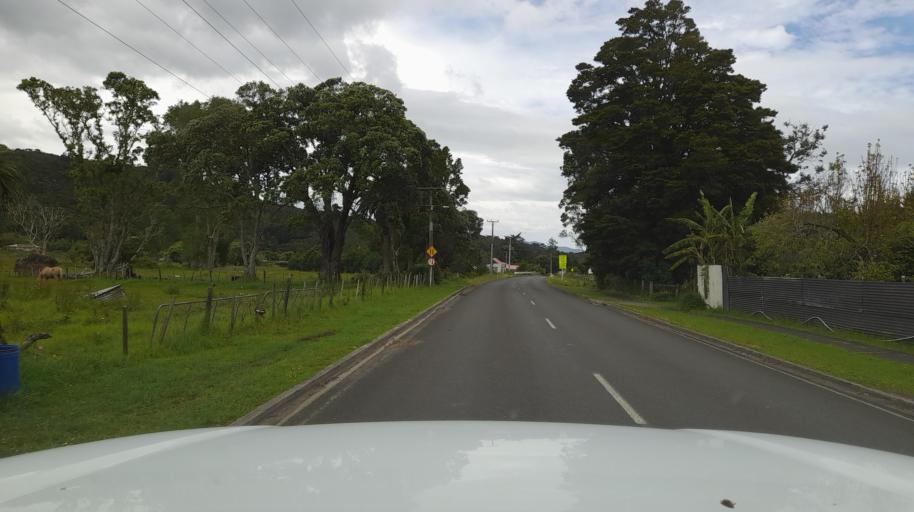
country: NZ
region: Northland
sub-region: Far North District
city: Kaitaia
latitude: -35.3789
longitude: 173.3828
